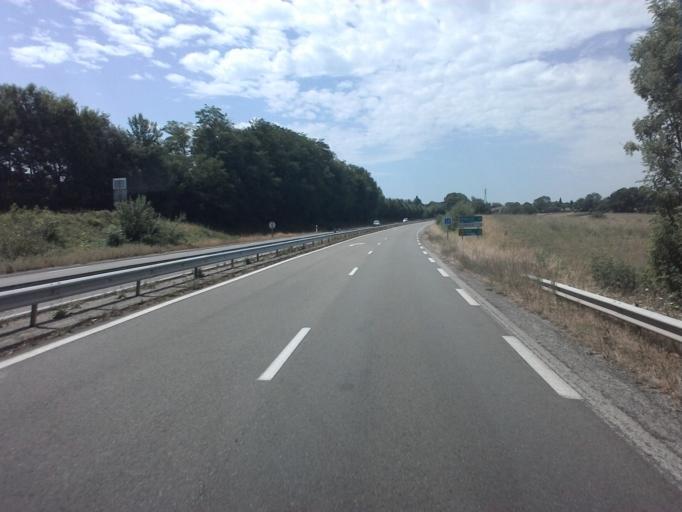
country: FR
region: Bourgogne
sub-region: Departement de Saone-et-Loire
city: Cuiseaux
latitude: 46.4893
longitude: 5.3754
